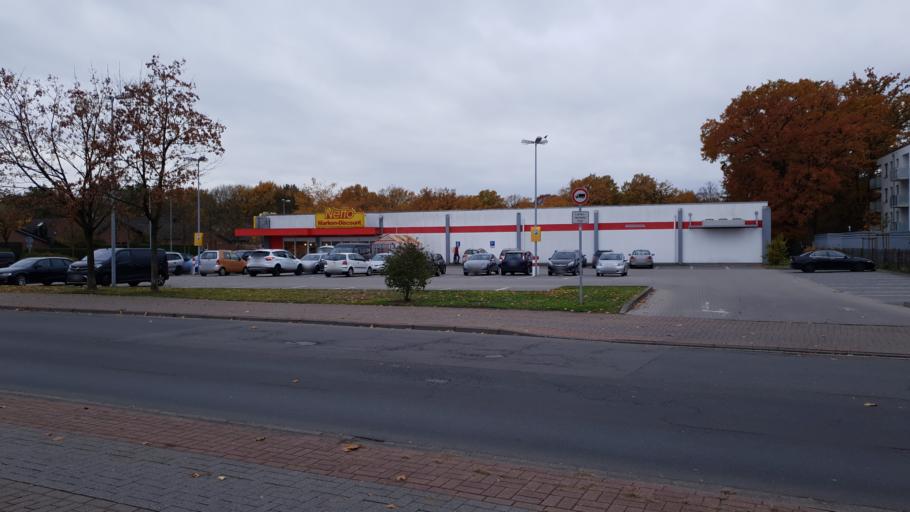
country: DE
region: Lower Saxony
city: Wardenburg
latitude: 53.1027
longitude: 8.2092
